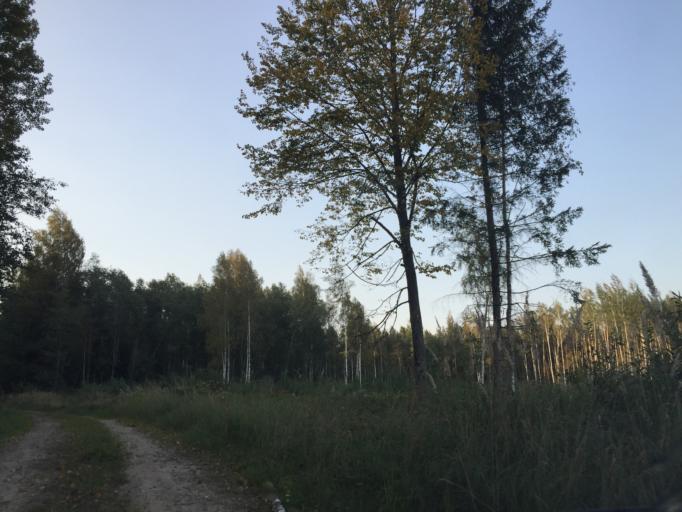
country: LV
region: Lielvarde
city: Lielvarde
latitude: 56.7882
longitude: 24.8356
